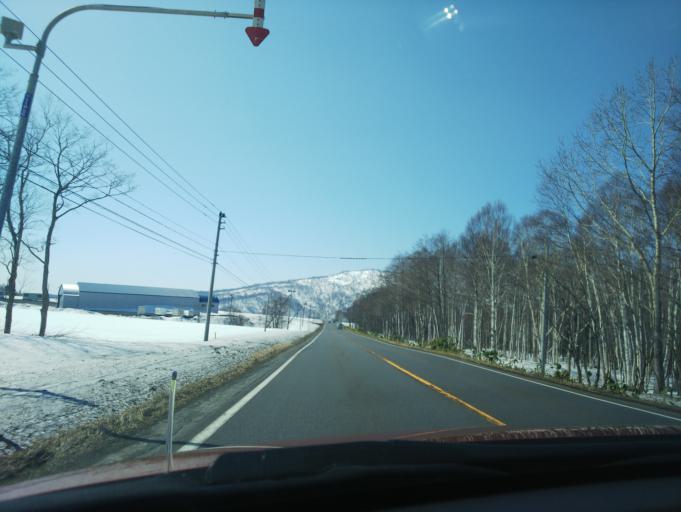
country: JP
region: Hokkaido
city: Nayoro
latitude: 44.6570
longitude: 142.2712
